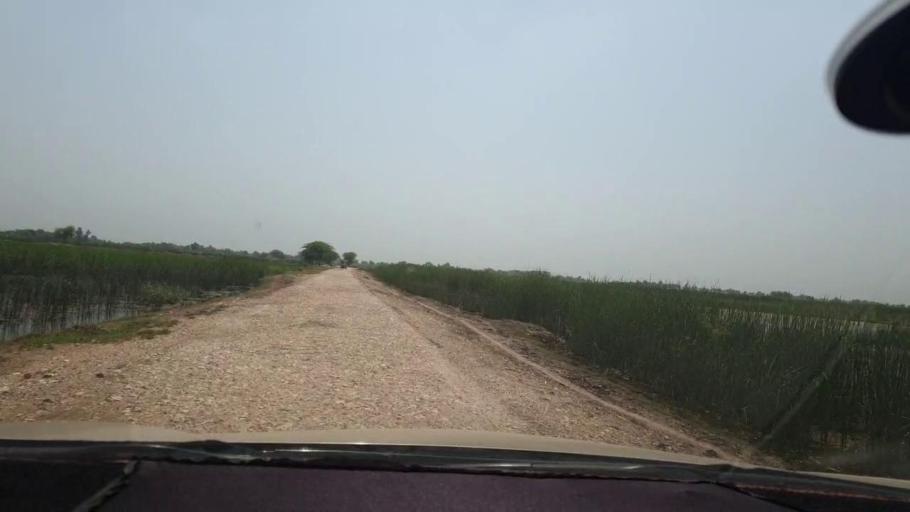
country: PK
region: Sindh
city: Kambar
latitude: 27.6480
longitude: 67.9320
